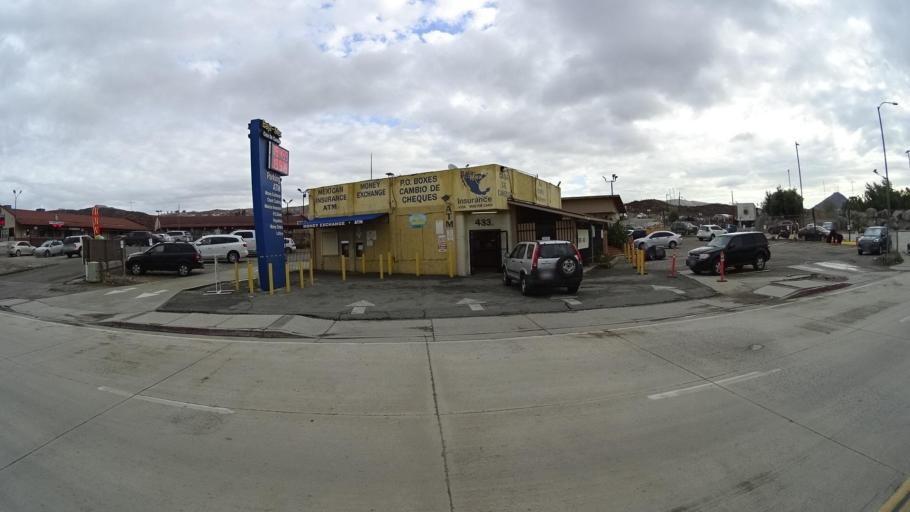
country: MX
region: Baja California
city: Tecate
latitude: 32.5782
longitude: -116.6282
